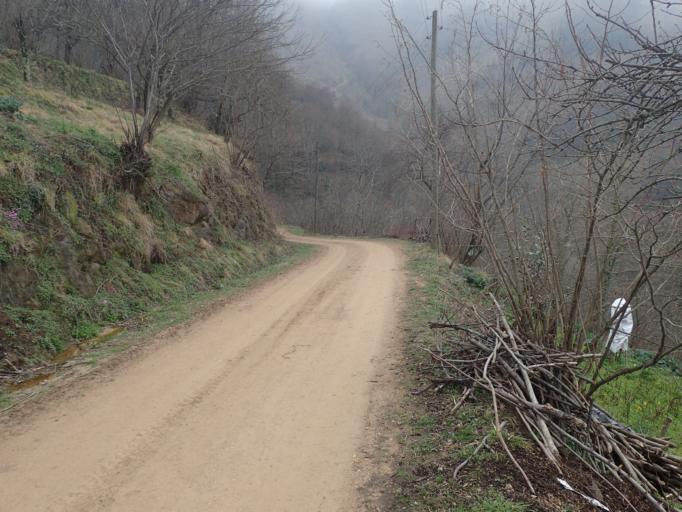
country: TR
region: Ordu
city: Camas
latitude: 40.9114
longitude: 37.5607
